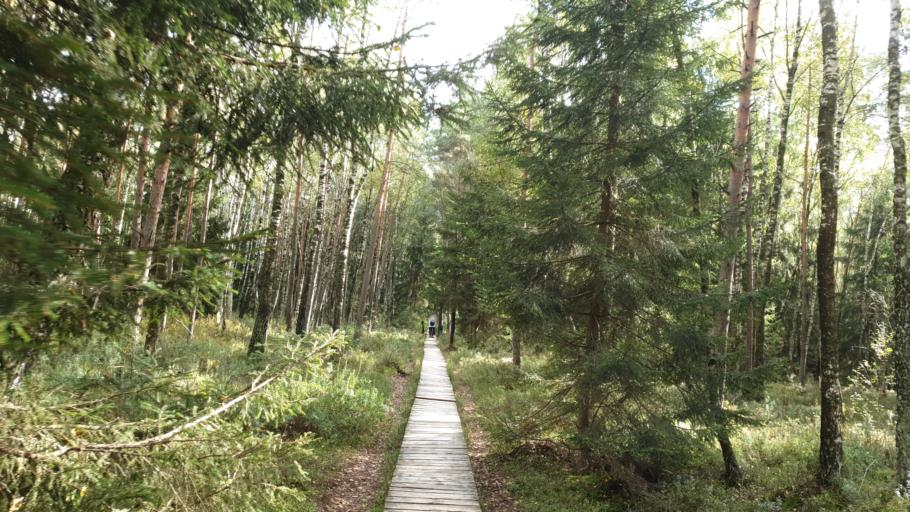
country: LT
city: Trakai
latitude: 54.6397
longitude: 24.9691
